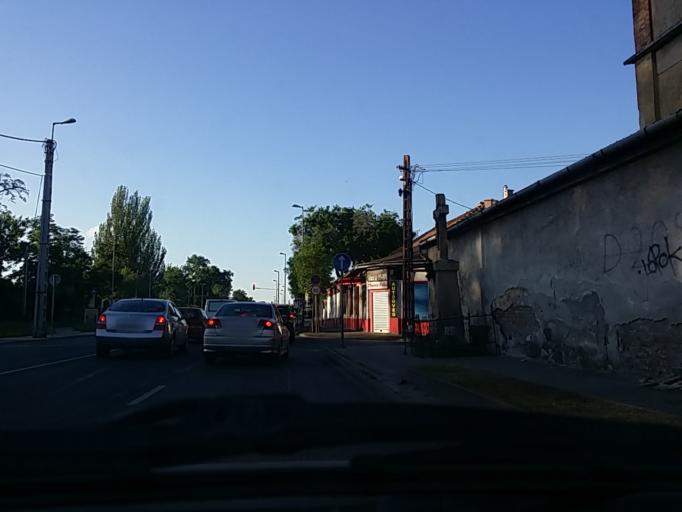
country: HU
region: Budapest
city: Budapest IV. keruelet
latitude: 47.5818
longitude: 19.0817
